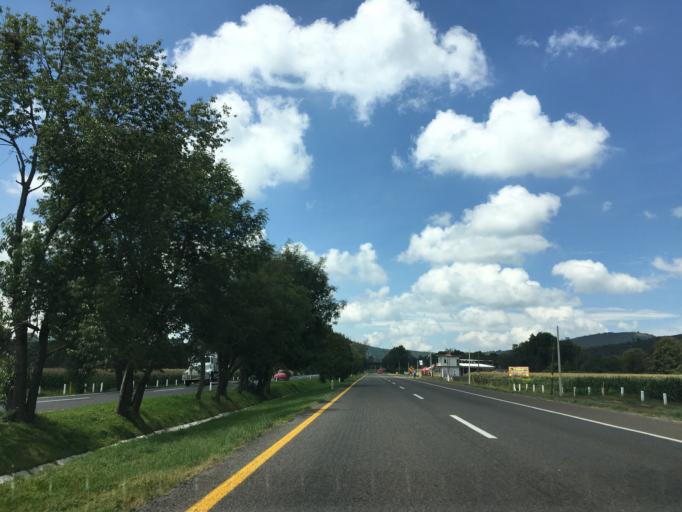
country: MX
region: Michoacan
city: Huiramba
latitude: 19.5461
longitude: -101.4457
